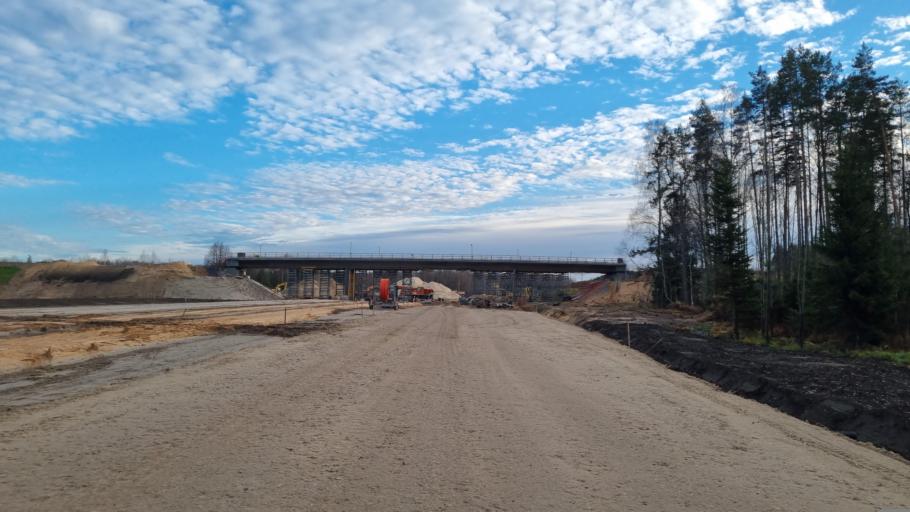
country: LV
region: Kekava
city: Kekava
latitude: 56.7798
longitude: 24.2382
